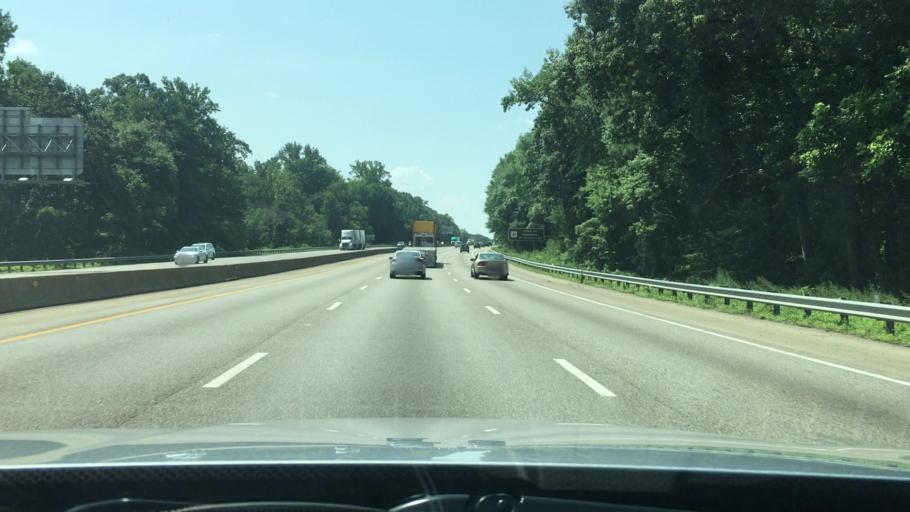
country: US
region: Virginia
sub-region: Chesterfield County
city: Chester
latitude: 37.3662
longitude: -77.4036
